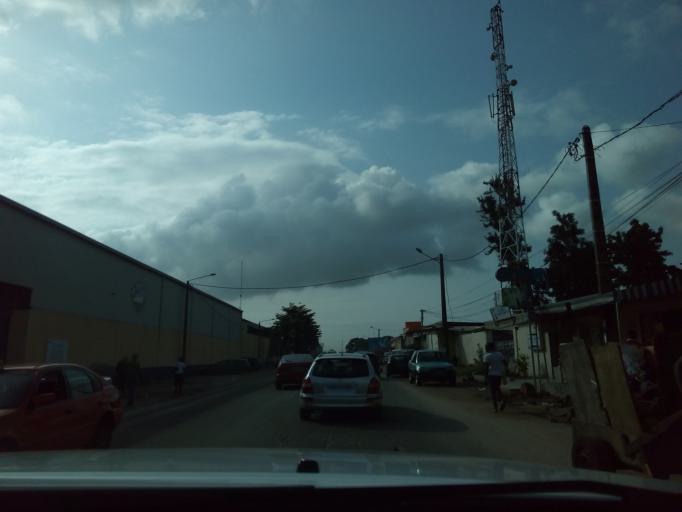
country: CI
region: Lagunes
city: Abidjan
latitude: 5.2942
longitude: -4.0015
